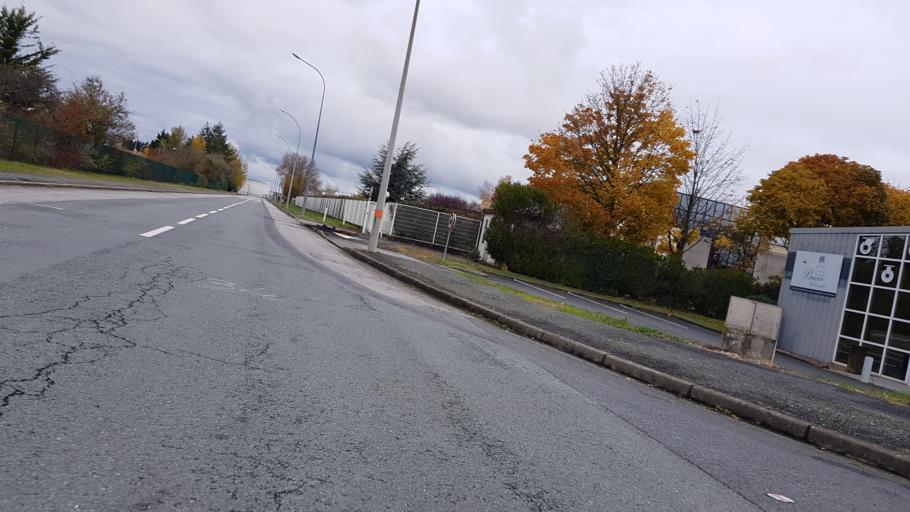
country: FR
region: Poitou-Charentes
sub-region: Departement de la Vienne
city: Chasseneuil-du-Poitou
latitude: 46.6594
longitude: 0.3718
